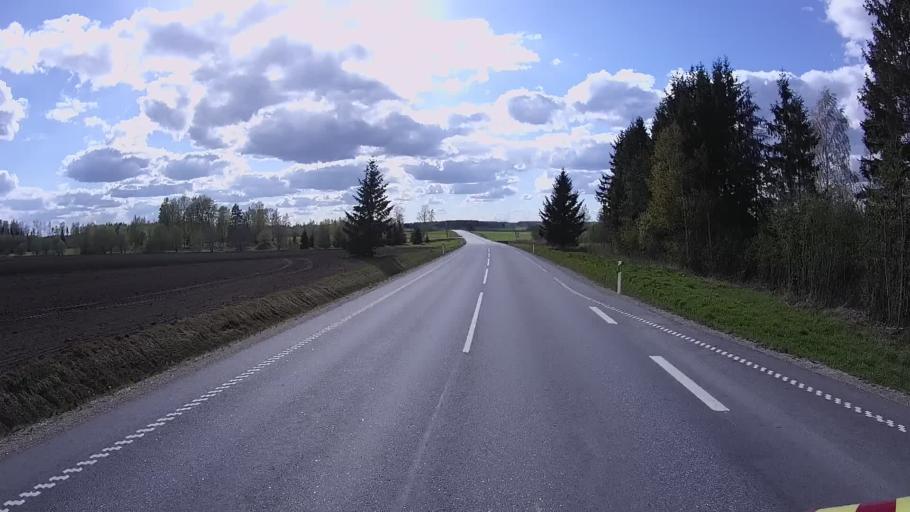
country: EE
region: Jogevamaa
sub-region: Mustvee linn
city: Mustvee
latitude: 58.8312
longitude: 26.7793
